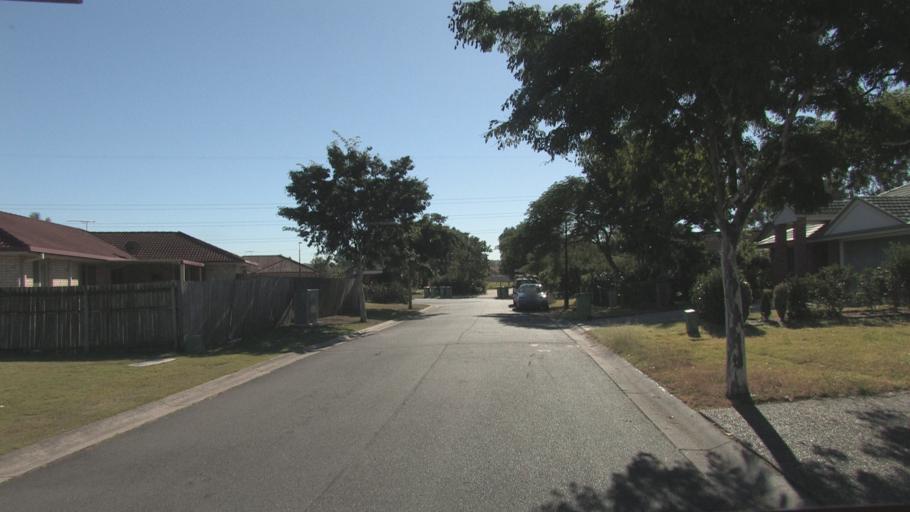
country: AU
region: Queensland
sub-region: Logan
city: Slacks Creek
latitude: -27.6607
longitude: 153.1459
